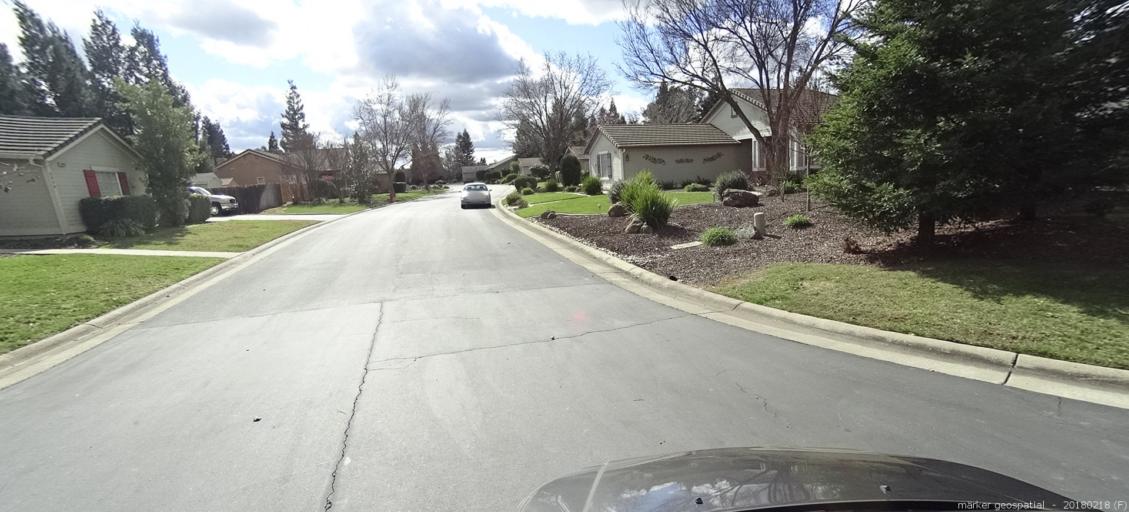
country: US
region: California
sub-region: Sacramento County
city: Orangevale
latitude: 38.6843
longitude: -121.2179
